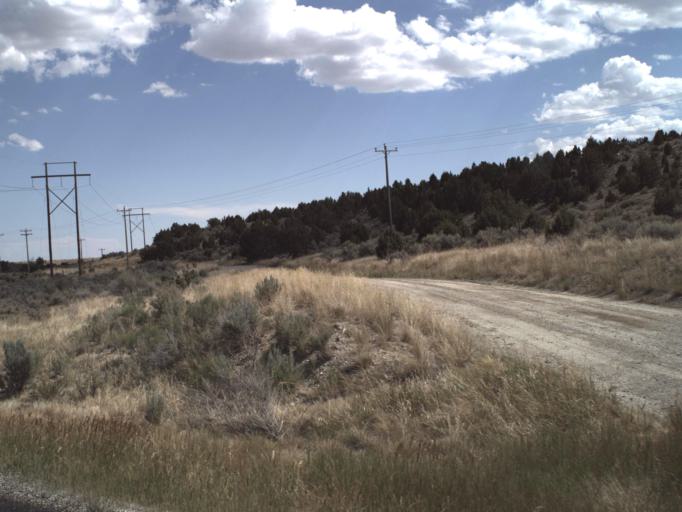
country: US
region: Idaho
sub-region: Minidoka County
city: Rupert
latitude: 41.9774
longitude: -113.1623
